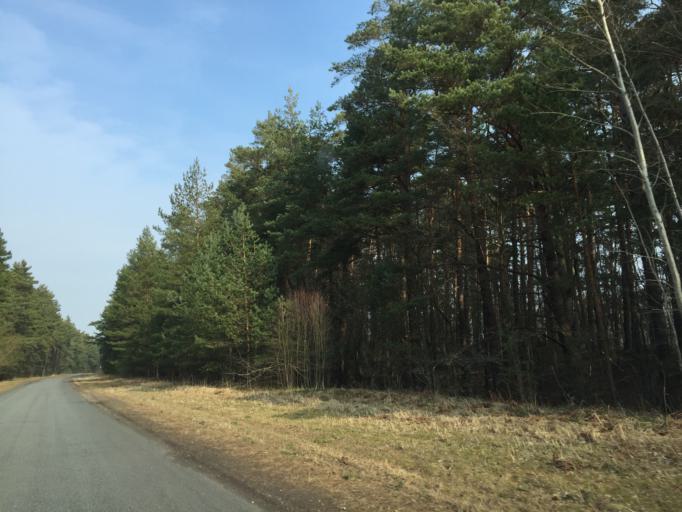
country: LV
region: Salacgrivas
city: Ainazi
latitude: 57.8873
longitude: 24.3678
